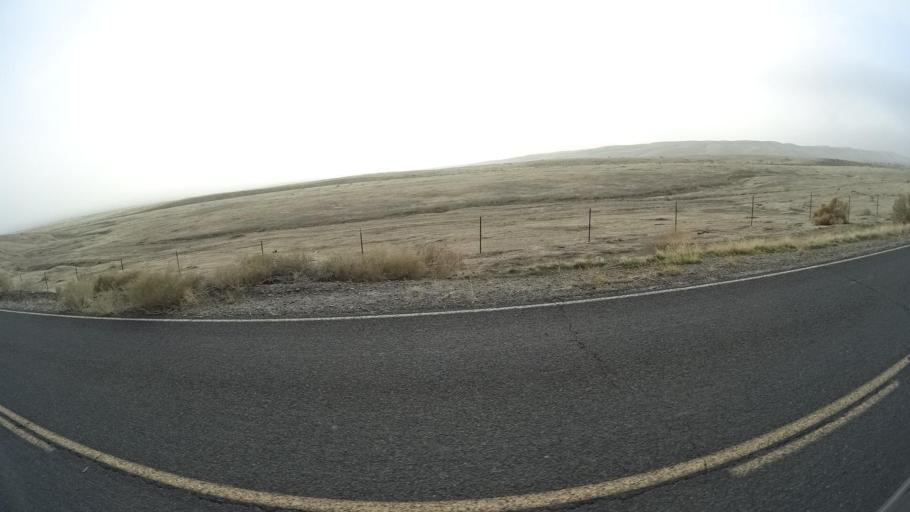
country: US
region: California
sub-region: Kern County
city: Ford City
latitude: 35.2421
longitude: -119.4539
